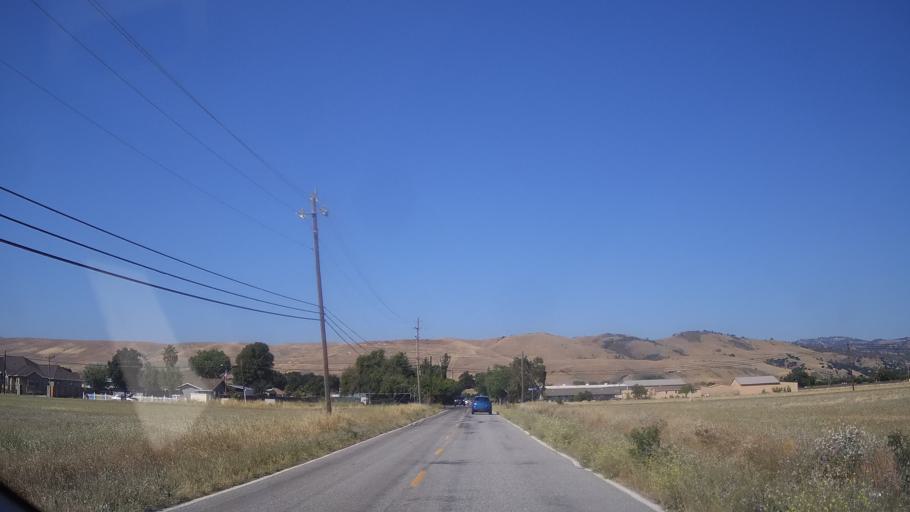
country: US
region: California
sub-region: Santa Clara County
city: Morgan Hill
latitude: 37.1648
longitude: -121.6928
